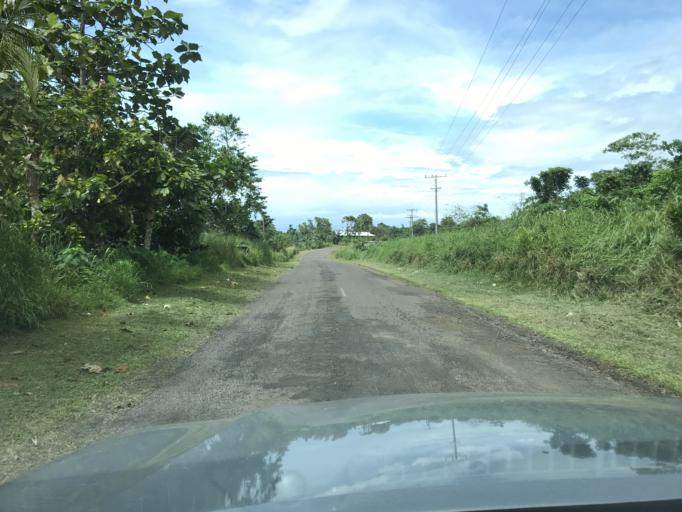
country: WS
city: Fasito`outa
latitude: -13.8609
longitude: -171.9098
